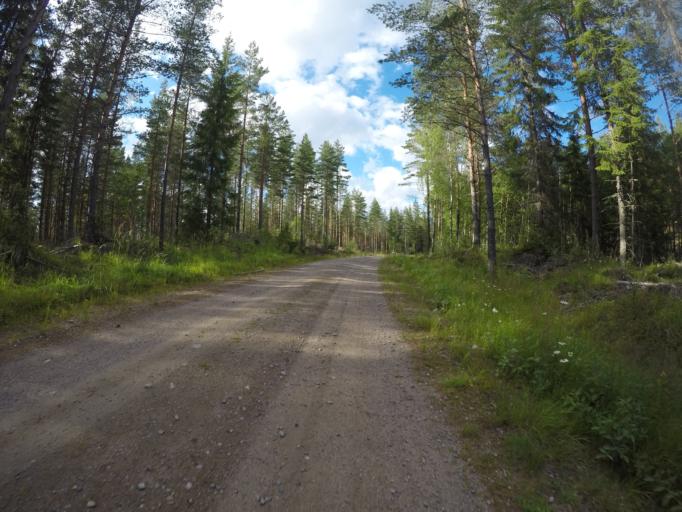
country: SE
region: OErebro
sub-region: Hallefors Kommun
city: Haellefors
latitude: 59.9621
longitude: 14.5615
